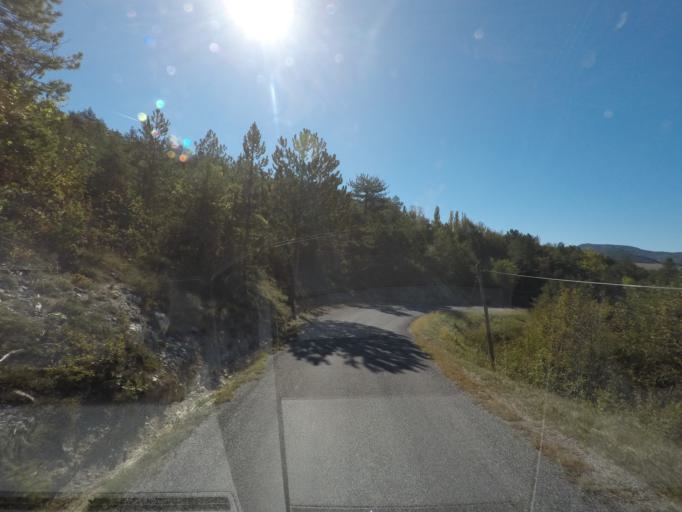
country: FR
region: Rhone-Alpes
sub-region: Departement de la Drome
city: Die
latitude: 44.5767
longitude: 5.2854
